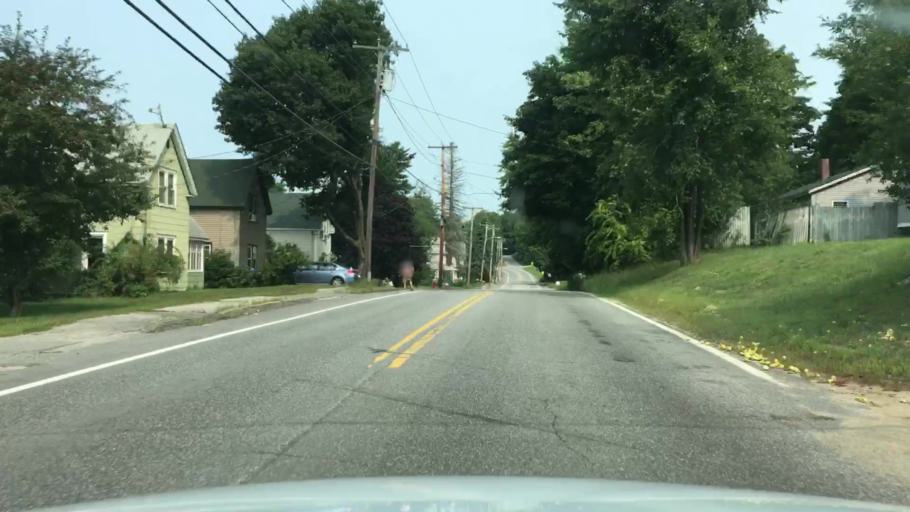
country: US
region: Maine
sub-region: Androscoggin County
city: Livermore Falls
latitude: 44.4665
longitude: -70.1822
